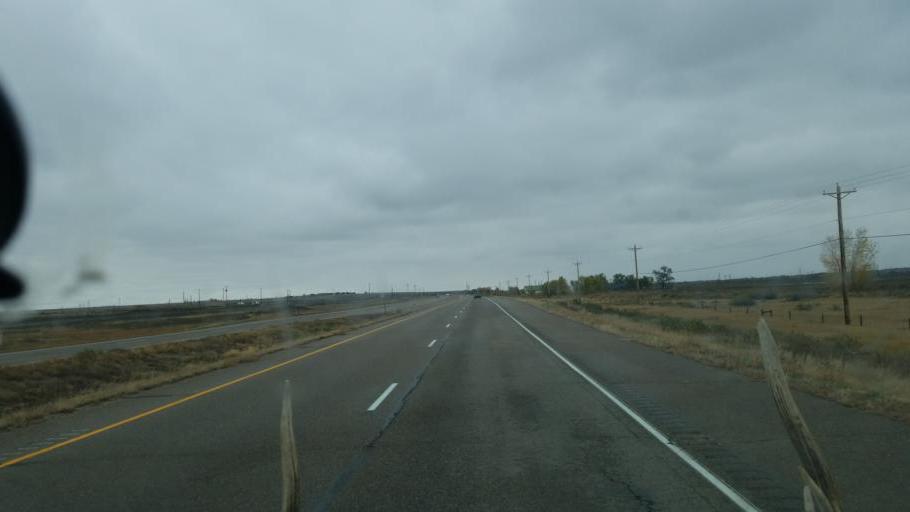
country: US
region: Colorado
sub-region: Pueblo County
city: Pueblo
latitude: 38.2698
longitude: -104.4063
